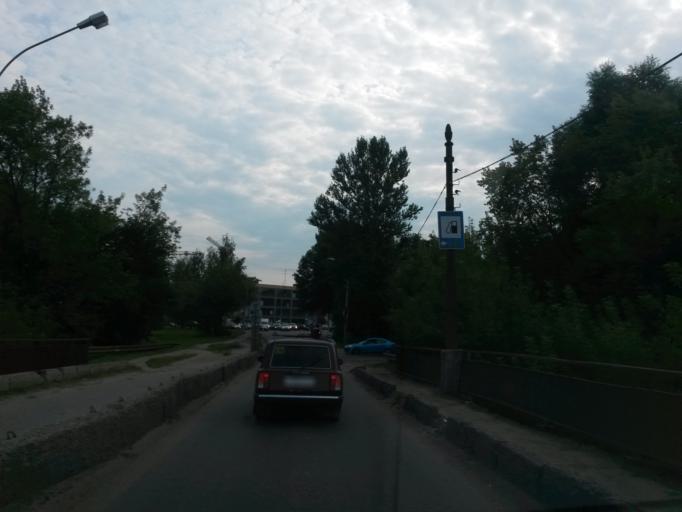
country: RU
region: Jaroslavl
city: Yaroslavl
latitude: 57.6097
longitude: 39.8370
